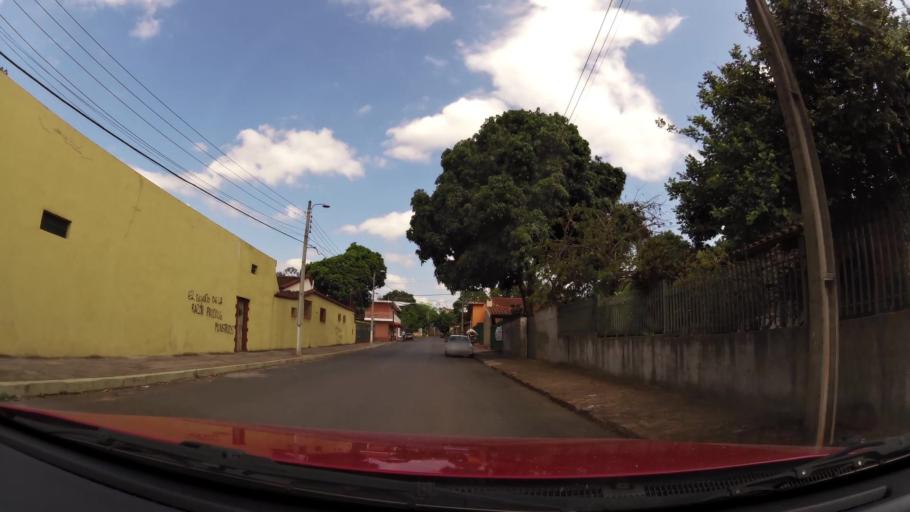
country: PY
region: Central
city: San Lorenzo
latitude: -25.3382
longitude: -57.5026
